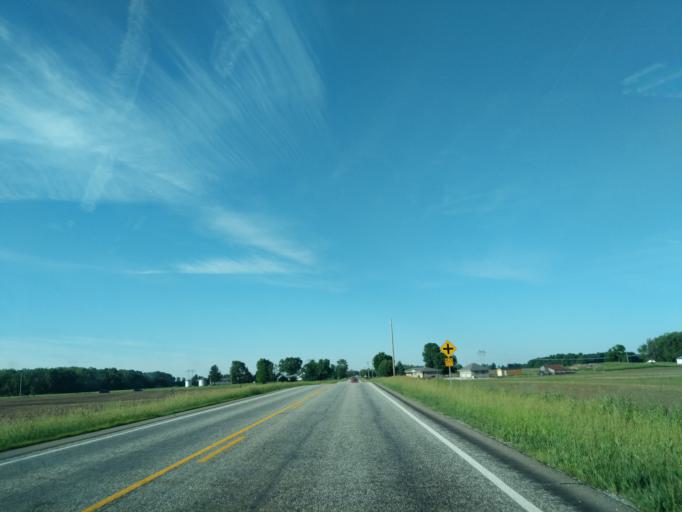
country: US
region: Indiana
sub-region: Madison County
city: Ingalls
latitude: 39.9475
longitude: -85.7665
